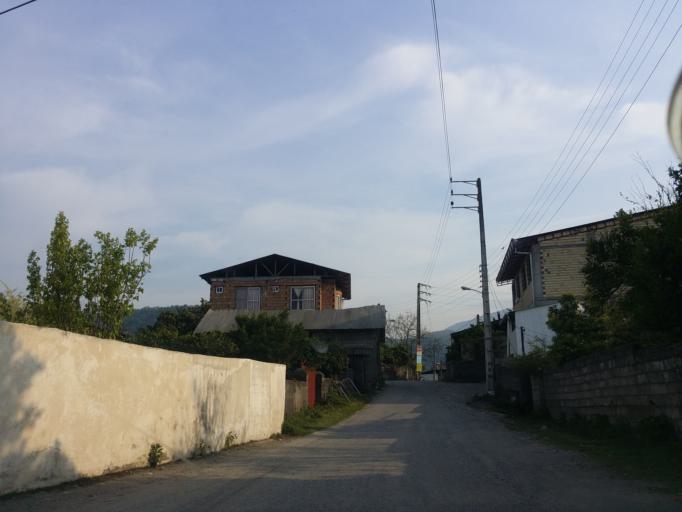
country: IR
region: Mazandaran
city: Chalus
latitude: 36.6564
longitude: 51.3672
